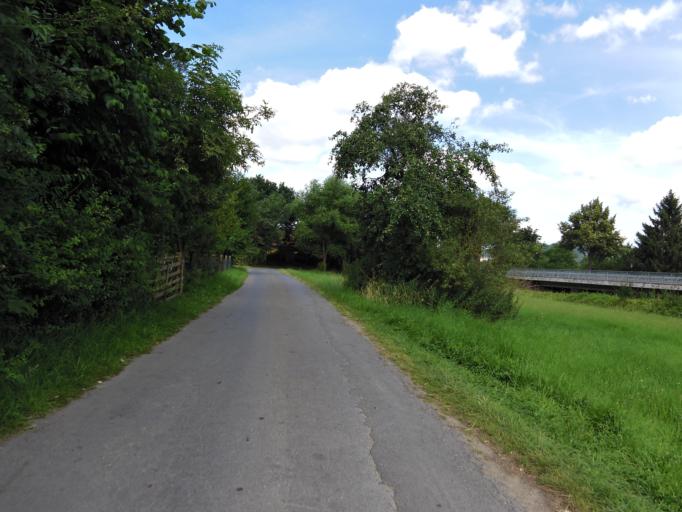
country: DE
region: North Rhine-Westphalia
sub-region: Regierungsbezirk Detmold
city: Hoexter
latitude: 51.7693
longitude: 9.3891
